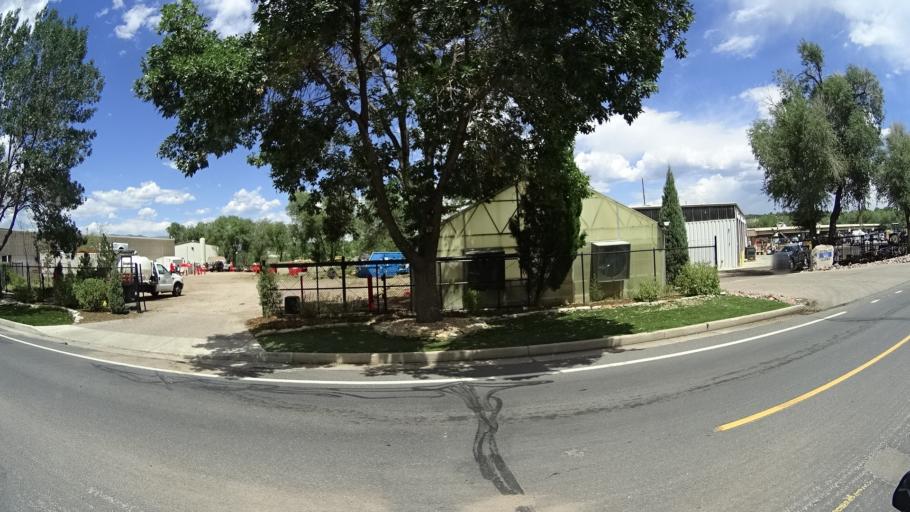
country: US
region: Colorado
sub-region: El Paso County
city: Colorado Springs
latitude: 38.8068
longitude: -104.8077
